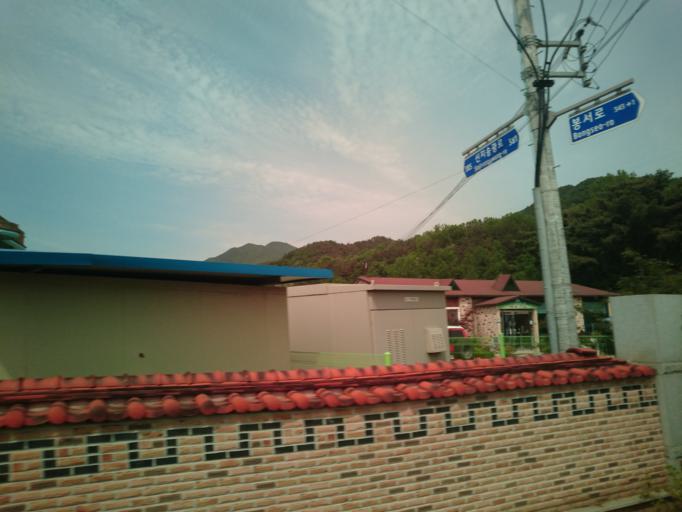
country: KR
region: Jeollabuk-do
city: Wanju
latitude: 35.8951
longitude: 127.1928
